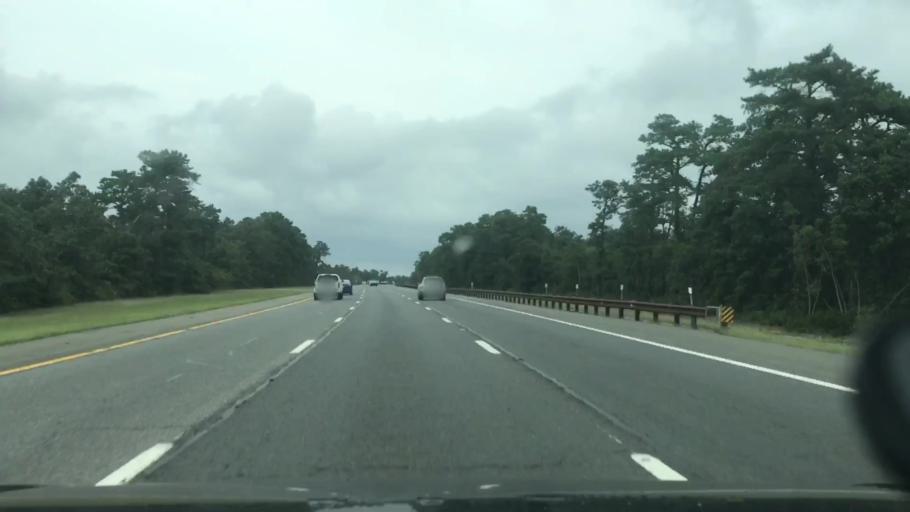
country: US
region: New Jersey
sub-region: Ocean County
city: Waretown
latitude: 39.8191
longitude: -74.2277
